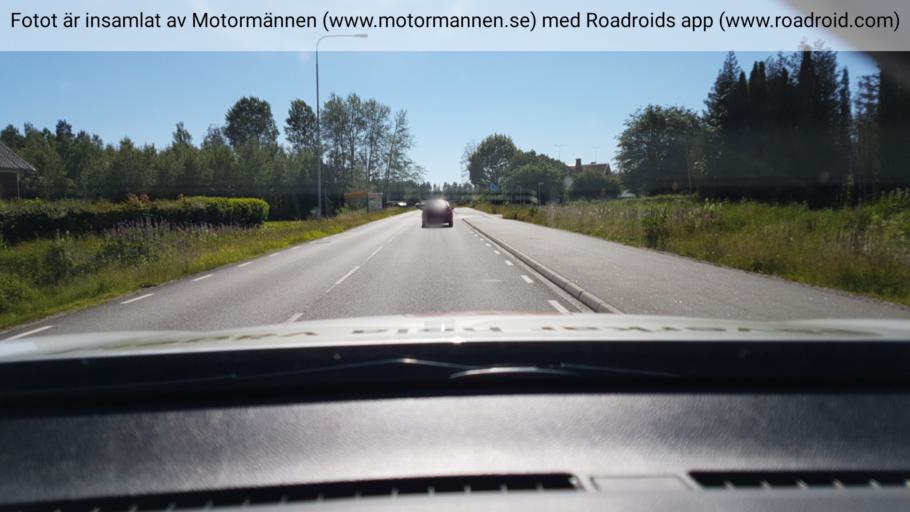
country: SE
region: OErebro
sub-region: Hallsbergs Kommun
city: Hallsberg
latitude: 59.1236
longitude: 15.0693
